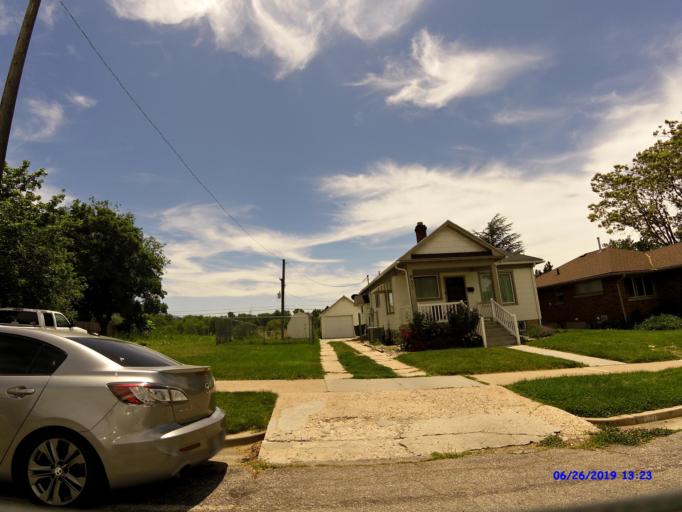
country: US
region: Utah
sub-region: Weber County
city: Ogden
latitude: 41.2090
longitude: -111.9556
